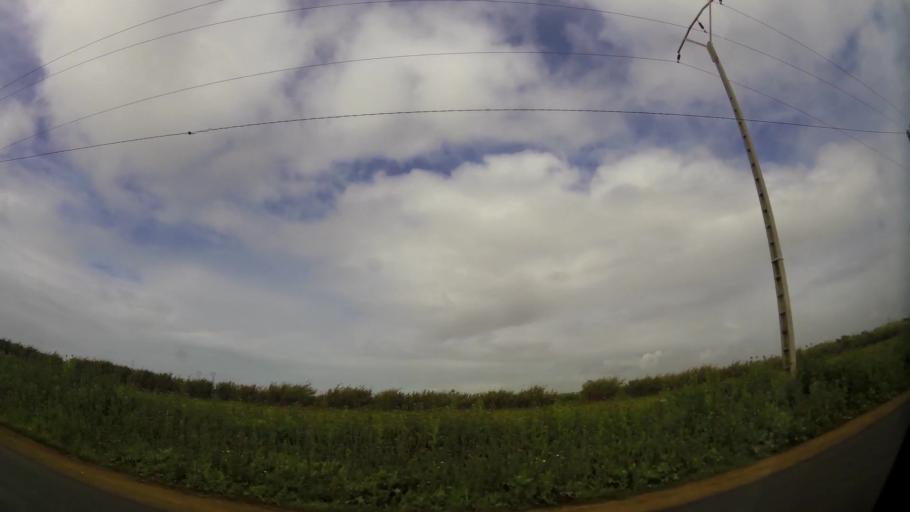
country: MA
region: Grand Casablanca
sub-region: Mohammedia
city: Mohammedia
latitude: 33.6492
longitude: -7.4563
